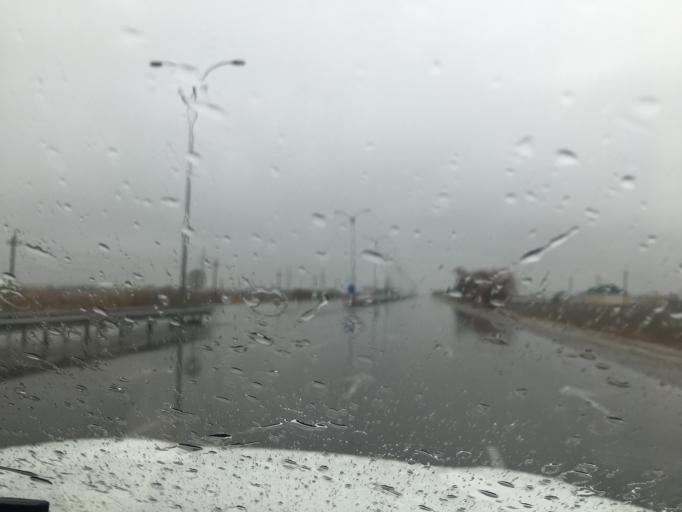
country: TM
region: Mary
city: Mary
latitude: 37.5418
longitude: 61.8758
